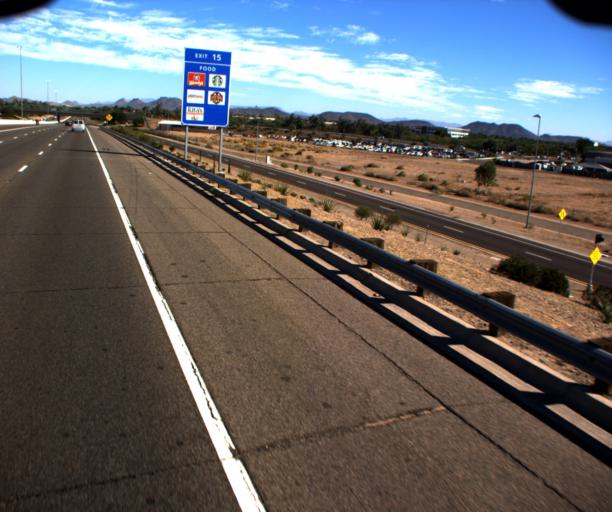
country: US
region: Arizona
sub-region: Maricopa County
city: Sun City
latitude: 33.6392
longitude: -112.2370
